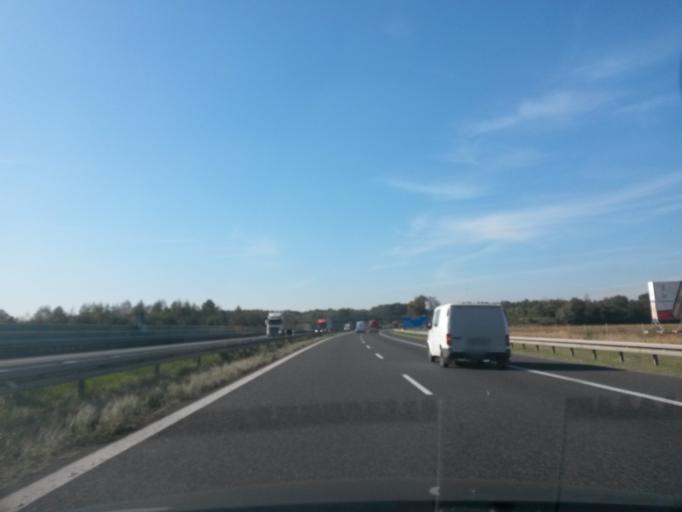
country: PL
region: Silesian Voivodeship
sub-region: Powiat gliwicki
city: Sosnicowice
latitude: 50.3494
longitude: 18.5327
